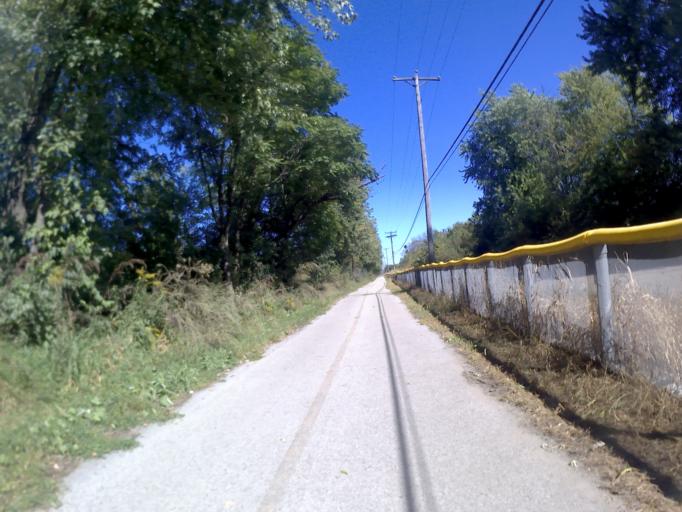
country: US
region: Illinois
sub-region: Cook County
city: Lemont
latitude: 41.6764
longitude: -88.0171
